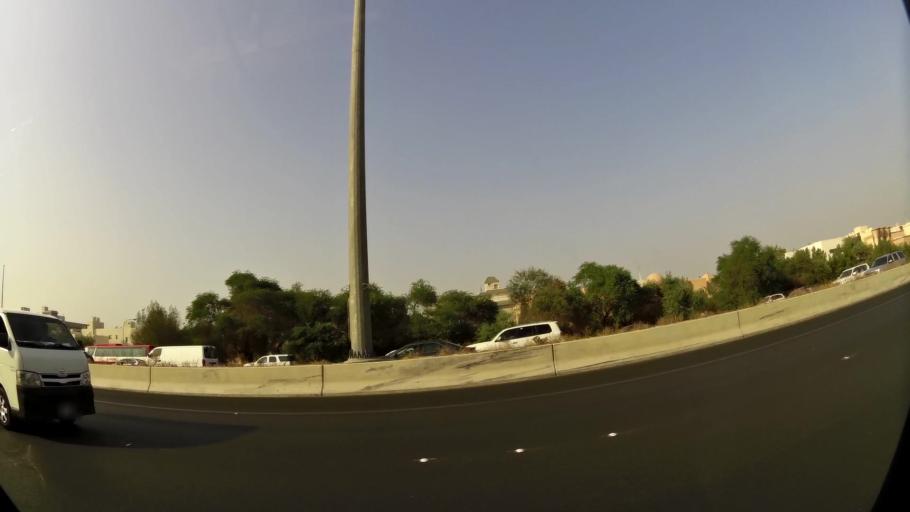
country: KW
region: Al Farwaniyah
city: Al Farwaniyah
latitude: 29.3033
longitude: 47.9724
